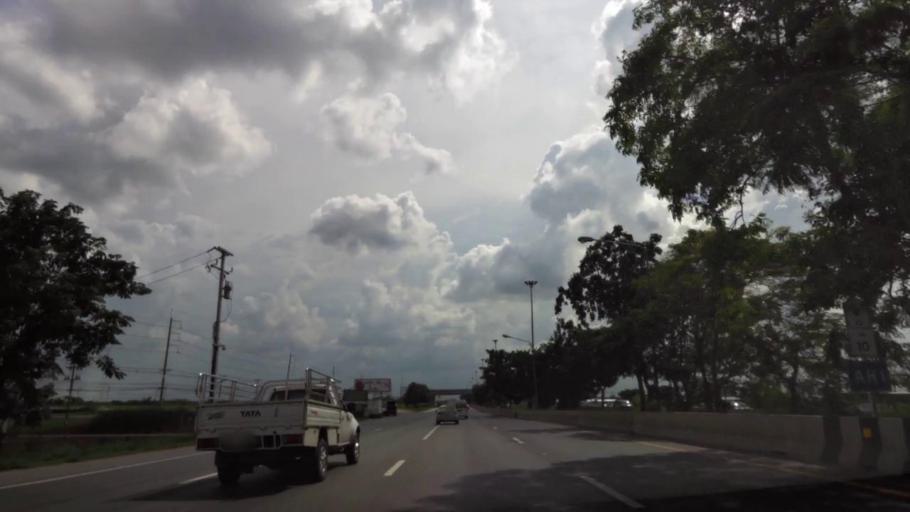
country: TH
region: Phra Nakhon Si Ayutthaya
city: Bang Pa-in
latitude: 14.2598
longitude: 100.6136
